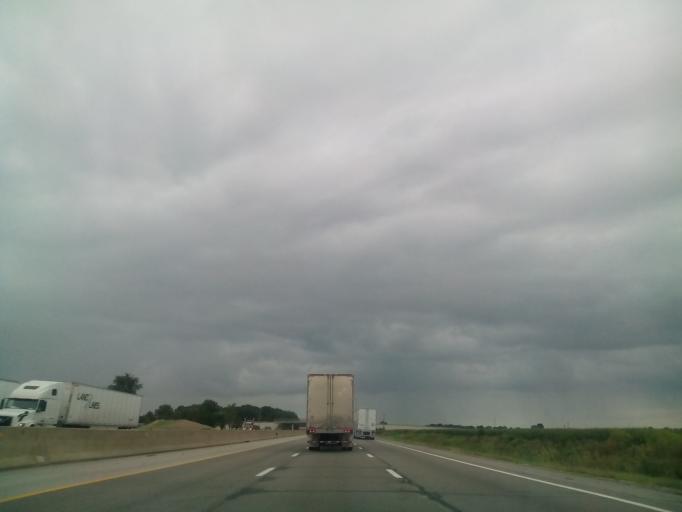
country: US
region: Ohio
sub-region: Sandusky County
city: Fremont
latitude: 41.3923
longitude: -83.0737
